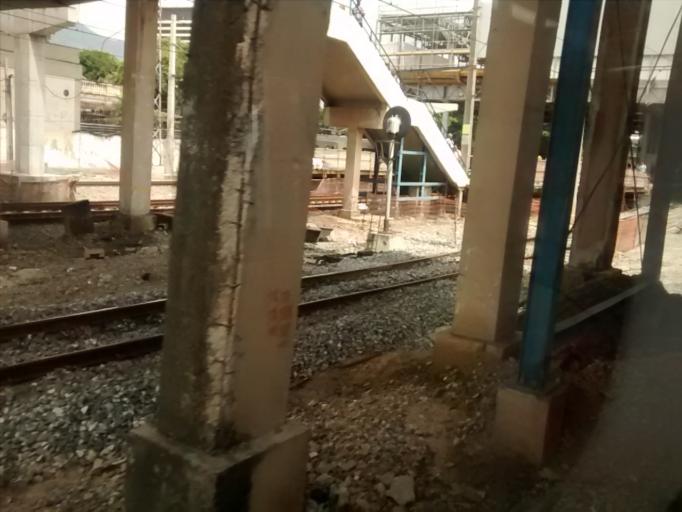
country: BR
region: Rio de Janeiro
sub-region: Rio De Janeiro
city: Rio de Janeiro
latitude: -22.9093
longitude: -43.2220
